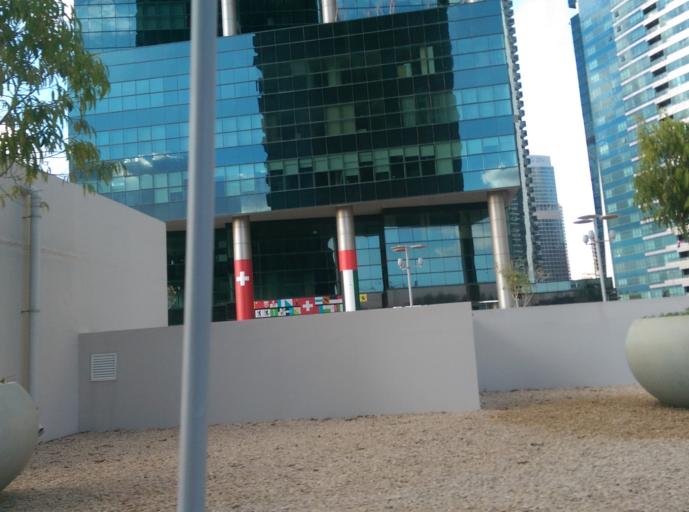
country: AE
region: Dubai
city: Dubai
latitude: 25.0781
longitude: 55.1535
